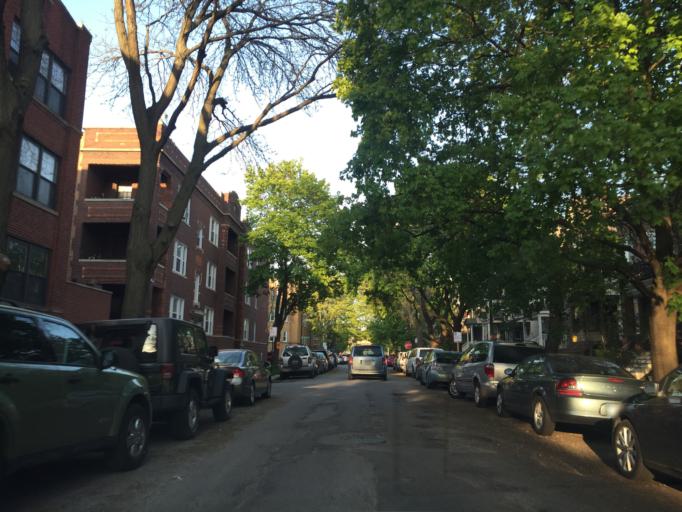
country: US
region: Illinois
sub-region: Cook County
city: Lincolnwood
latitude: 41.9667
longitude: -87.6910
